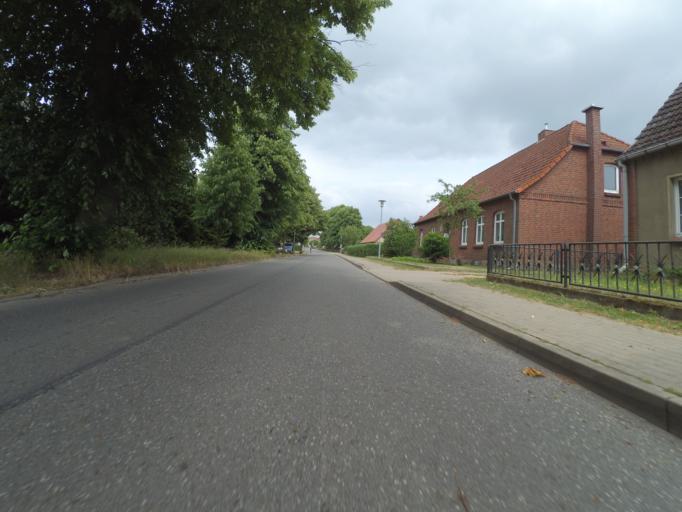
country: DE
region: Mecklenburg-Vorpommern
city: Lubz
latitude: 53.4098
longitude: 12.0555
